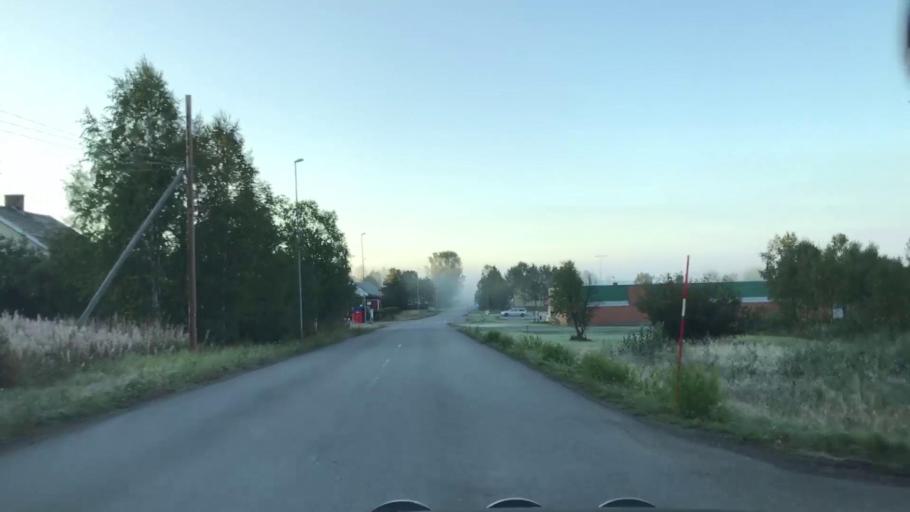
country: SE
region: Norrbotten
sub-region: Gallivare Kommun
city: Malmberget
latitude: 67.6494
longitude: 21.0453
